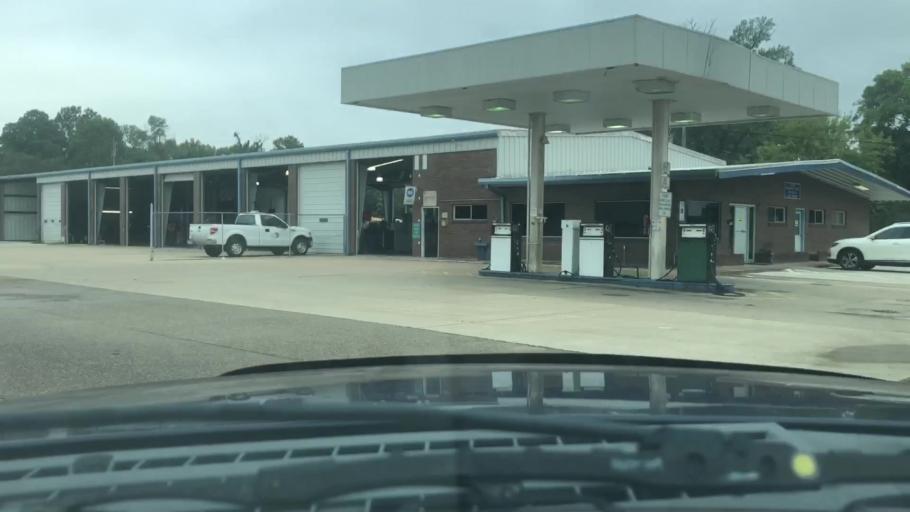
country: US
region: Texas
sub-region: Bowie County
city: Texarkana
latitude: 33.4260
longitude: -94.0528
